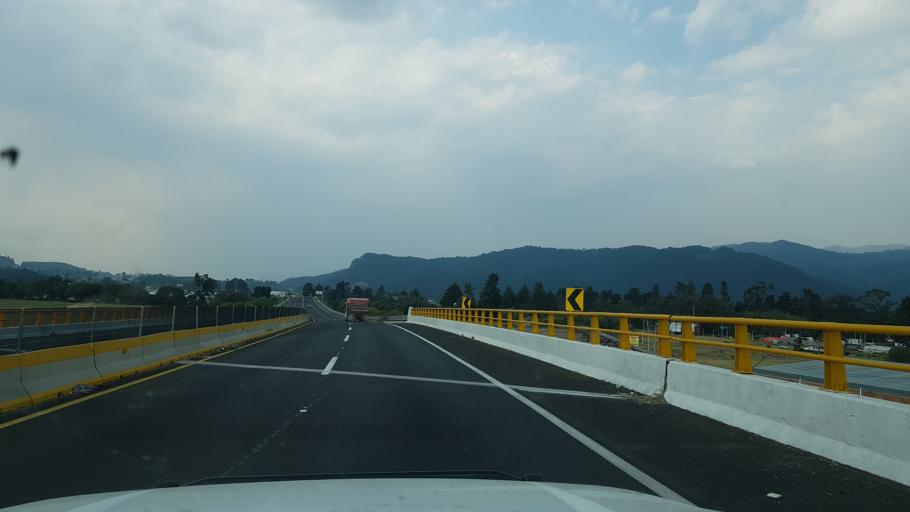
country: MX
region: Mexico
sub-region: Ayapango
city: La Colonia
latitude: 19.1393
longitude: -98.7761
